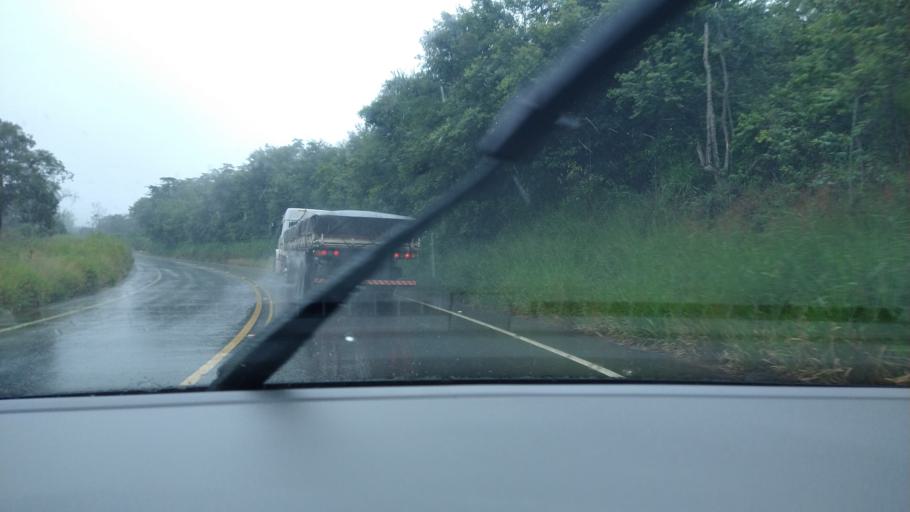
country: BR
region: Minas Gerais
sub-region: Ponte Nova
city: Ponte Nova
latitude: -20.5715
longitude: -42.8723
